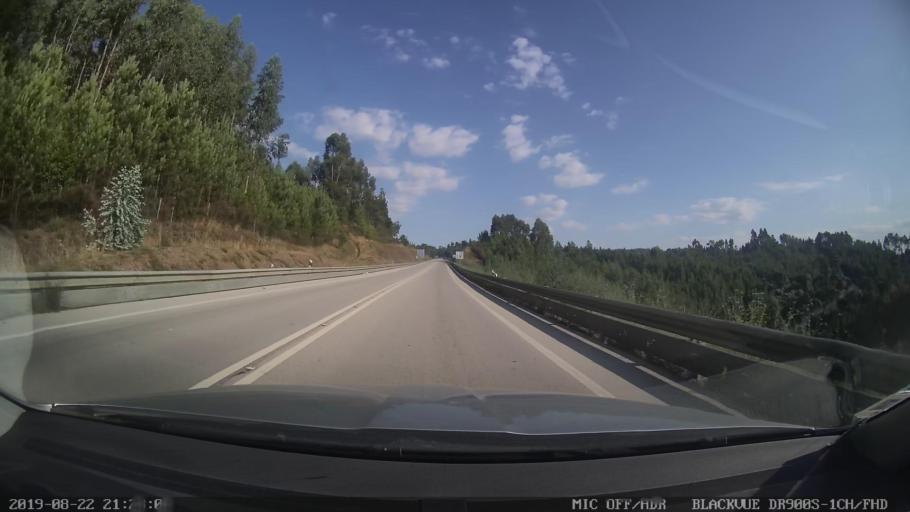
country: PT
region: Castelo Branco
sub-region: Serta
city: Serta
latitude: 39.8256
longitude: -8.1068
